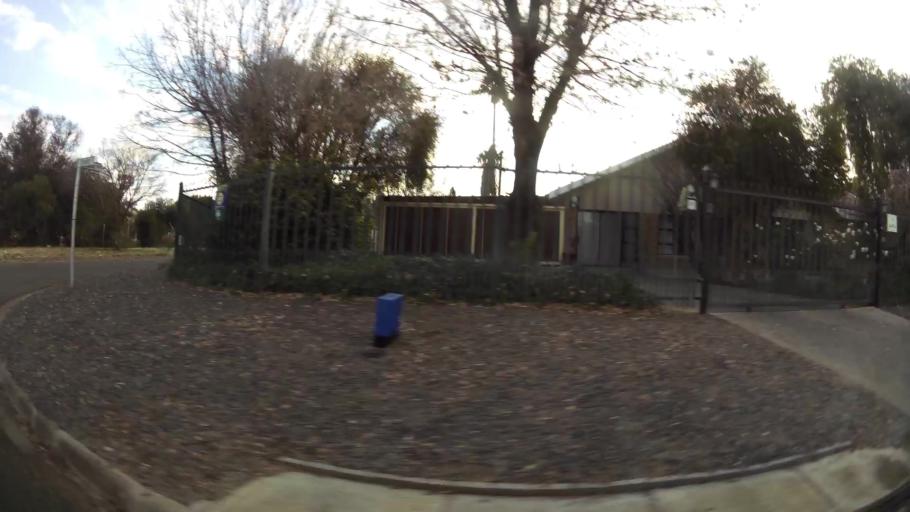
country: ZA
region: Orange Free State
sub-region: Mangaung Metropolitan Municipality
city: Bloemfontein
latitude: -29.1474
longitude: 26.1747
